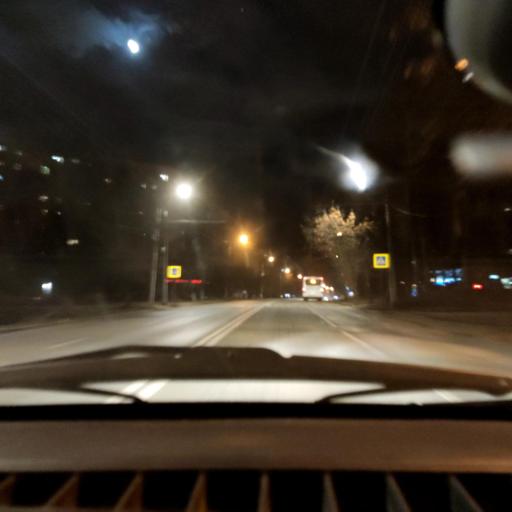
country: RU
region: Bashkortostan
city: Ufa
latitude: 54.7476
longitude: 56.0237
